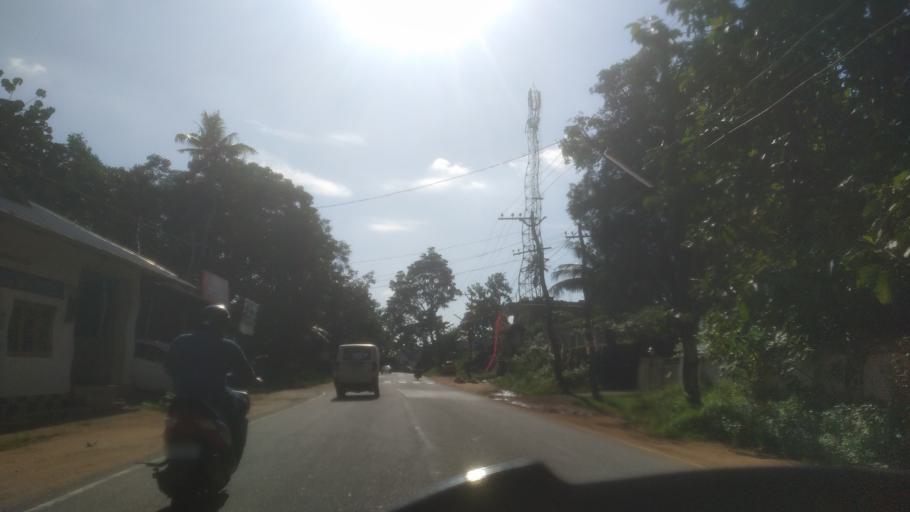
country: IN
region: Kerala
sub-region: Ernakulam
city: Muvattupuzha
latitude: 9.9804
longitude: 76.5536
